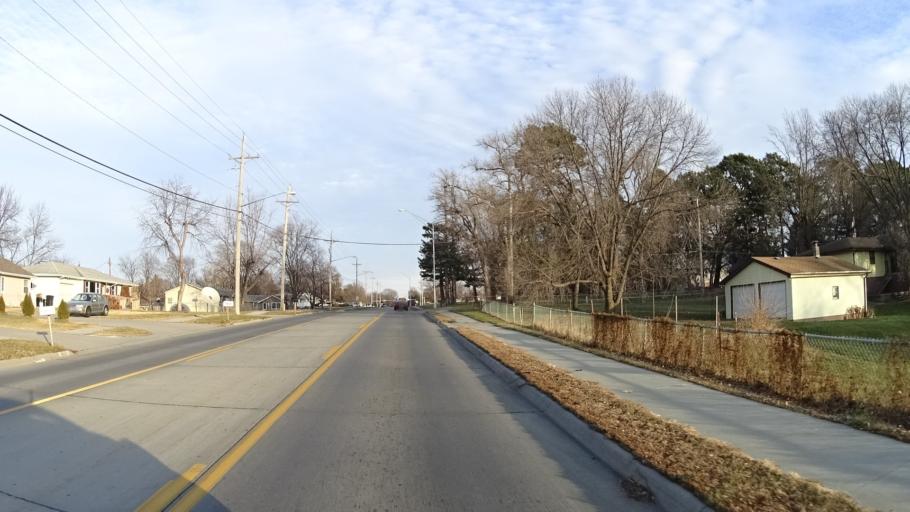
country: US
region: Nebraska
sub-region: Sarpy County
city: La Vista
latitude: 41.1907
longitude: -95.9908
